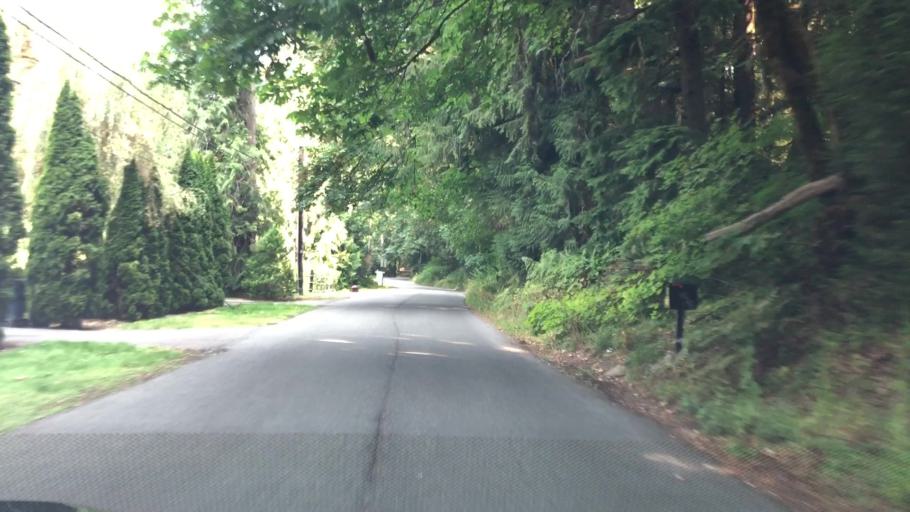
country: US
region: Washington
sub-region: King County
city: Cottage Lake
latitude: 47.7511
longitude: -122.0785
